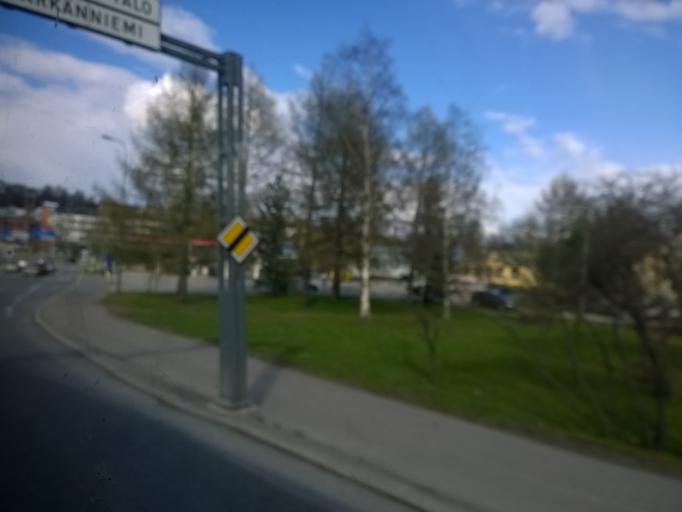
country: FI
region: Pirkanmaa
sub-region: Tampere
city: Tampere
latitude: 61.4887
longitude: 23.7795
